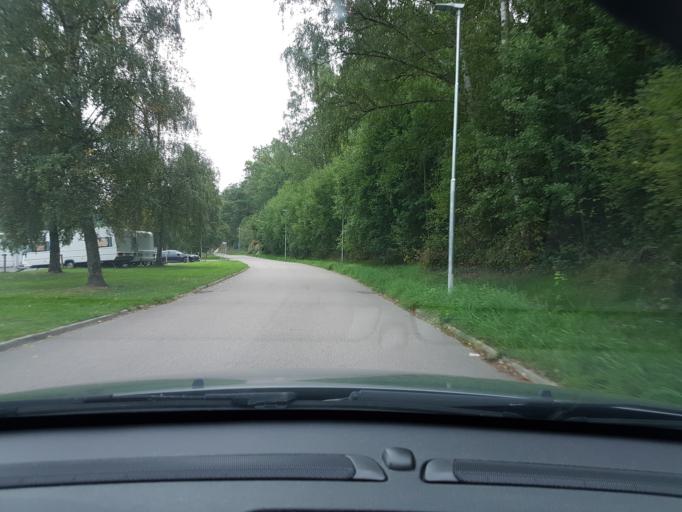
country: SE
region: Vaestra Goetaland
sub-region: Ale Kommun
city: Nodinge-Nol
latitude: 57.9120
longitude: 12.0666
